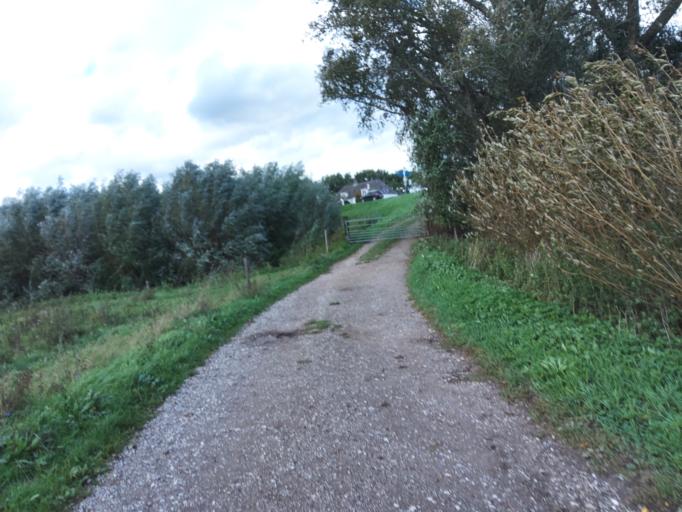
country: NL
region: Gelderland
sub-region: Gemeente Neerijnen
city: Neerijnen
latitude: 51.8284
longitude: 5.2796
